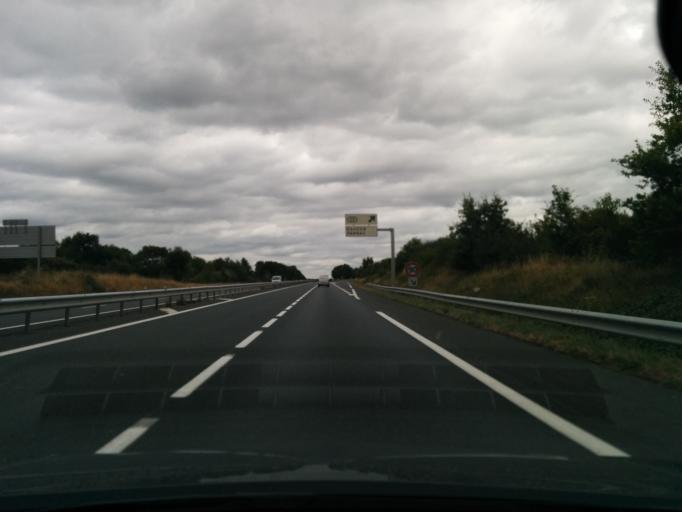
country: FR
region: Centre
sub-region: Departement de l'Indre
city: Chantome
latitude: 46.4330
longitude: 1.4778
